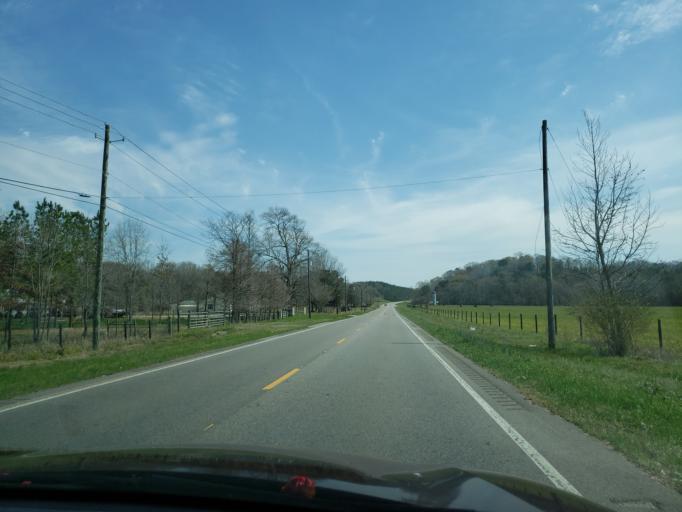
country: US
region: Alabama
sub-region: Autauga County
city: Prattville
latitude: 32.4328
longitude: -86.5719
